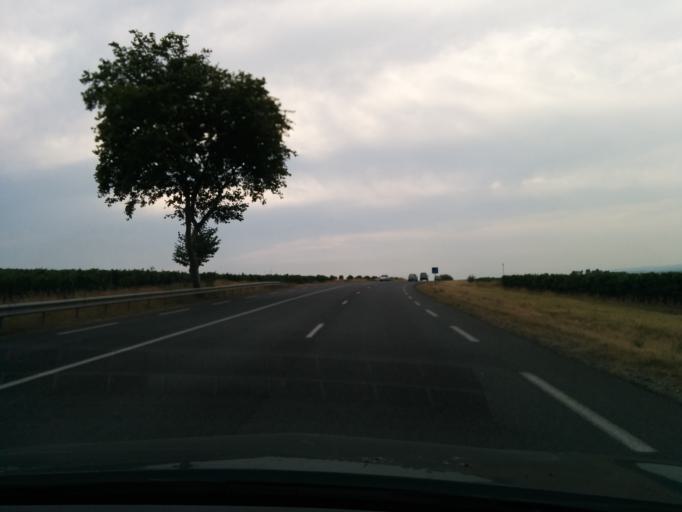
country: FR
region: Languedoc-Roussillon
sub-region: Departement de l'Aude
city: Pennautier
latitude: 43.2423
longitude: 2.3040
